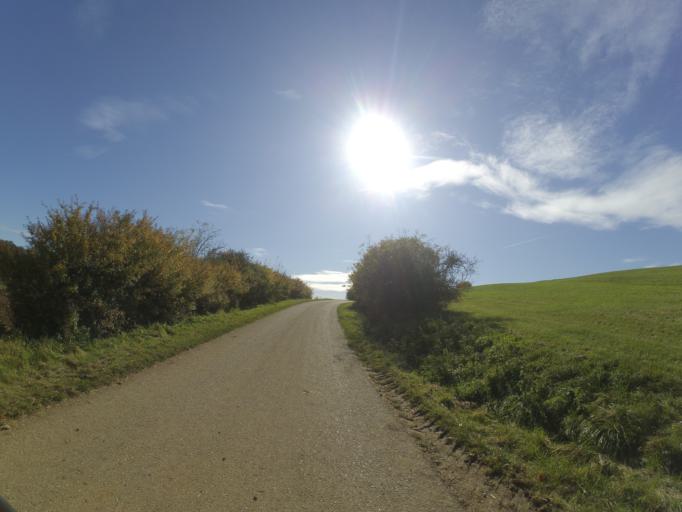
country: DE
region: Baden-Wuerttemberg
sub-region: Tuebingen Region
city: Westerstetten
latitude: 48.5409
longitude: 9.9602
